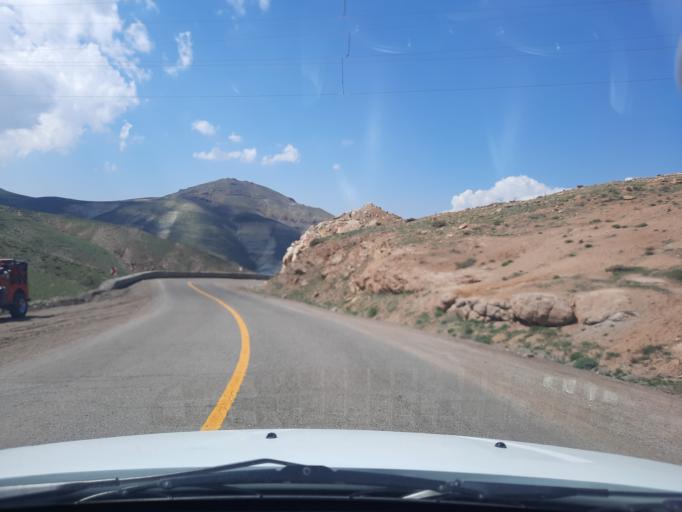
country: IR
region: Qazvin
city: Qazvin
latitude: 36.3948
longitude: 50.2112
